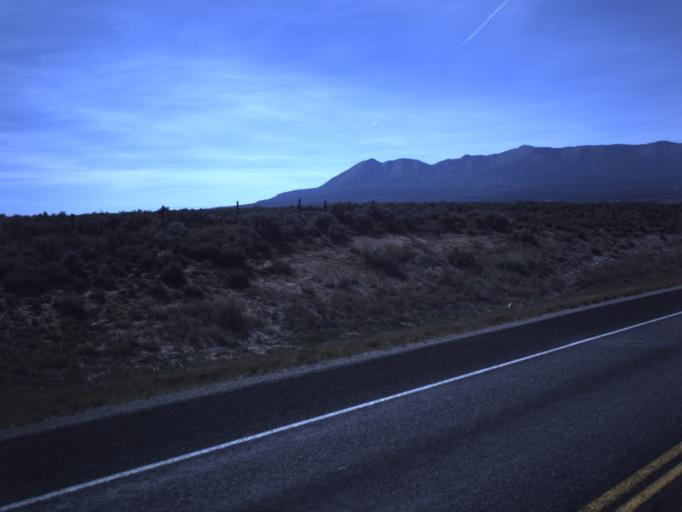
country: US
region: Utah
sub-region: San Juan County
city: Monticello
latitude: 37.8691
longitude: -109.2471
